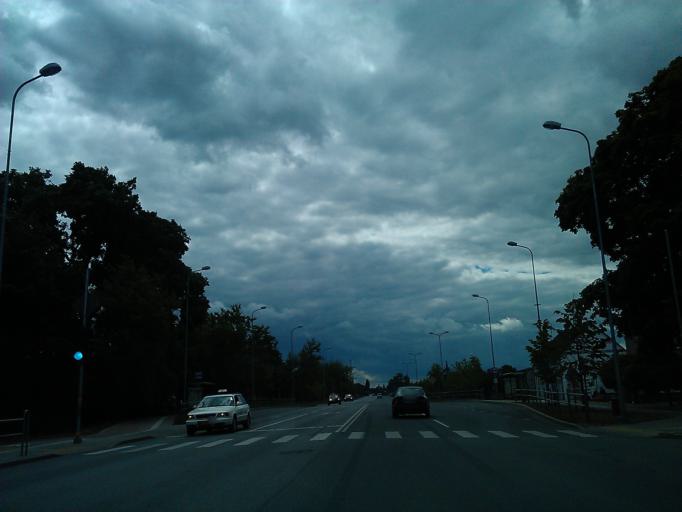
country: LV
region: Jelgava
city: Jelgava
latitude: 56.6354
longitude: 23.7281
